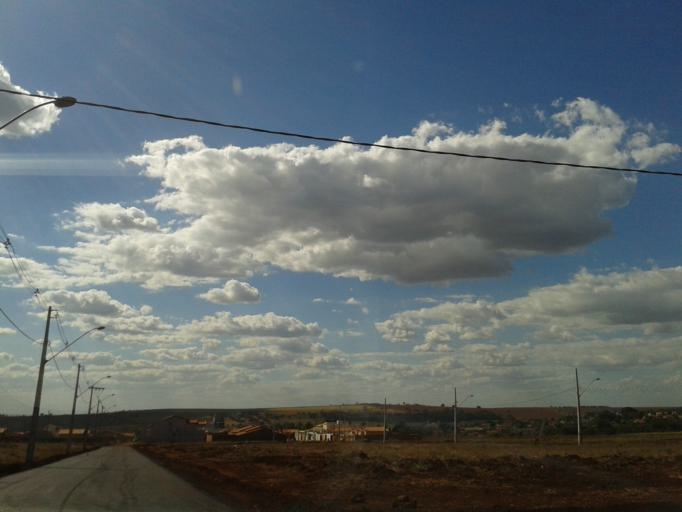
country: BR
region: Minas Gerais
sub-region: Capinopolis
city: Capinopolis
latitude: -18.6954
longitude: -49.5763
